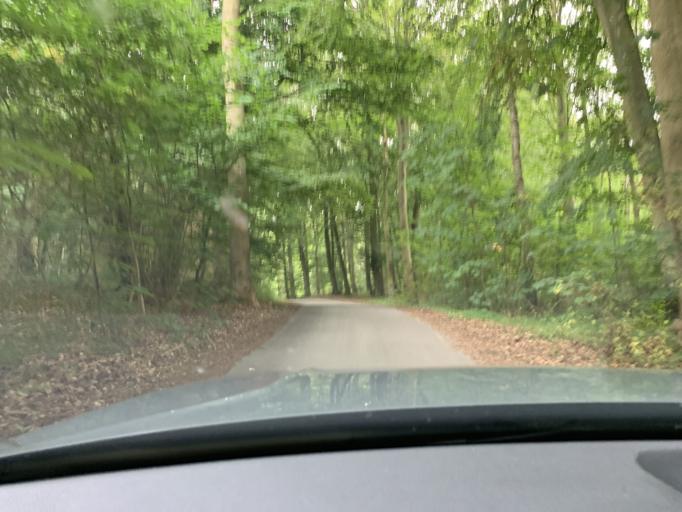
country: DK
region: Zealand
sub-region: Guldborgsund Kommune
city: Norre Alslev
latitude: 54.8485
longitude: 11.9346
